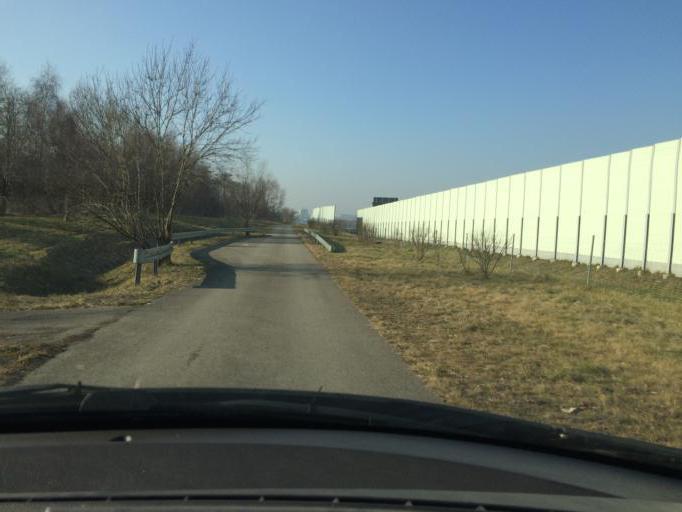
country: PL
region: Lesser Poland Voivodeship
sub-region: Powiat wielicki
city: Czarnochowice
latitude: 50.0058
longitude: 20.0410
